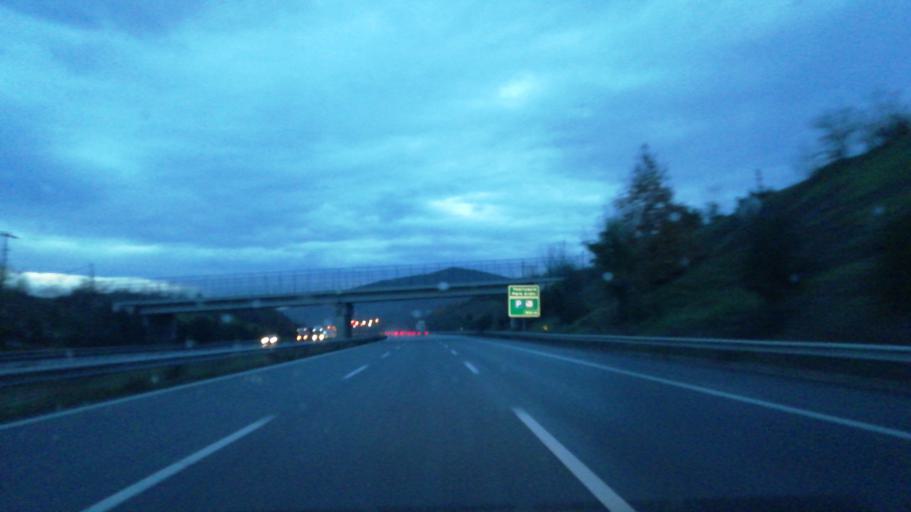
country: TR
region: Sakarya
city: Karadere
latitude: 40.8078
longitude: 30.8683
